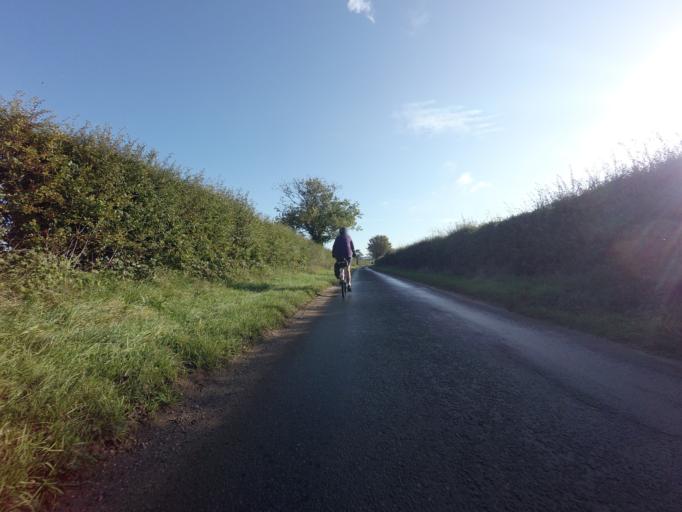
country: GB
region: England
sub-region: Norfolk
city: Dersingham
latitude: 52.8231
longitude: 0.5385
